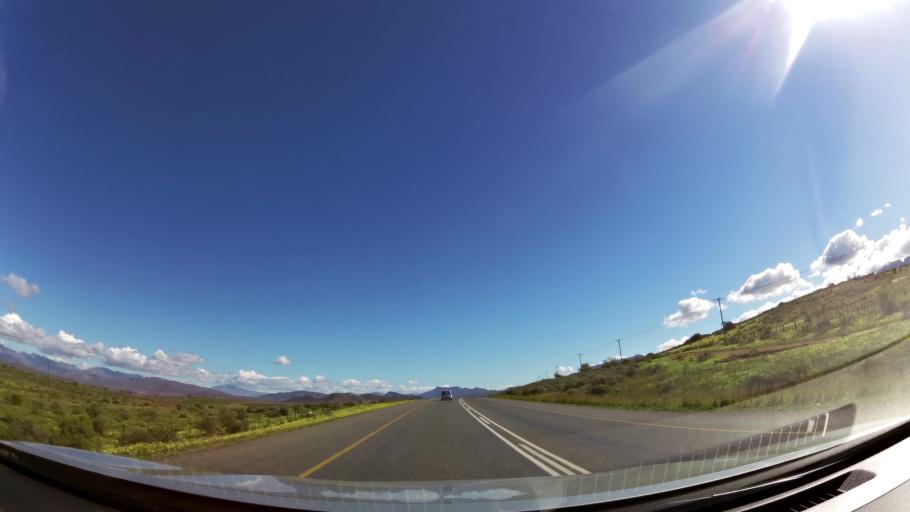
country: ZA
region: Western Cape
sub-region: Cape Winelands District Municipality
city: Ashton
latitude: -33.8177
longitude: 19.9515
